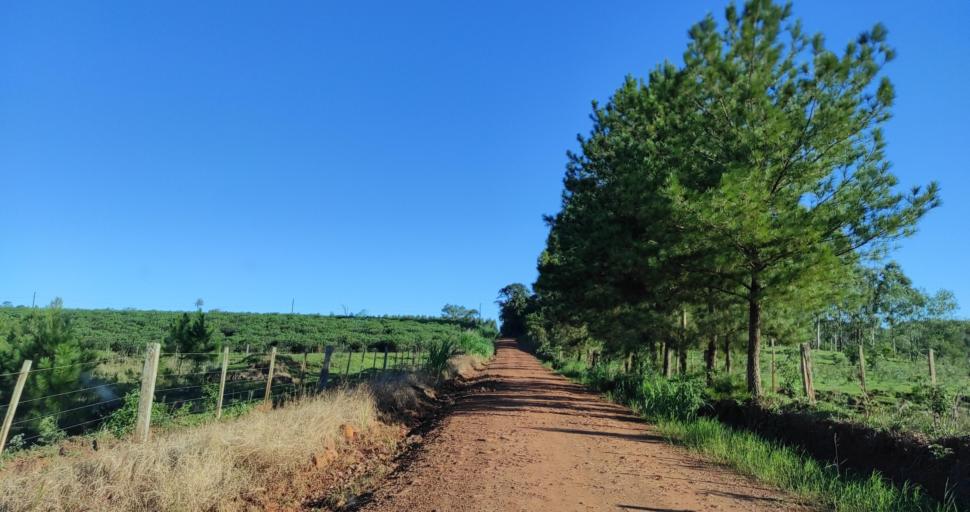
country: AR
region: Misiones
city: Puerto Rico
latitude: -26.8507
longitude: -55.0137
